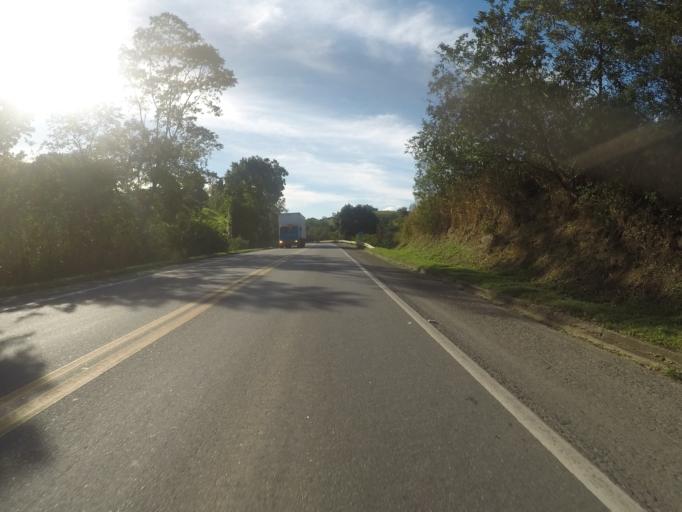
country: BR
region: Espirito Santo
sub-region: Fundao
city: Fundao
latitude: -19.8948
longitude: -40.4118
